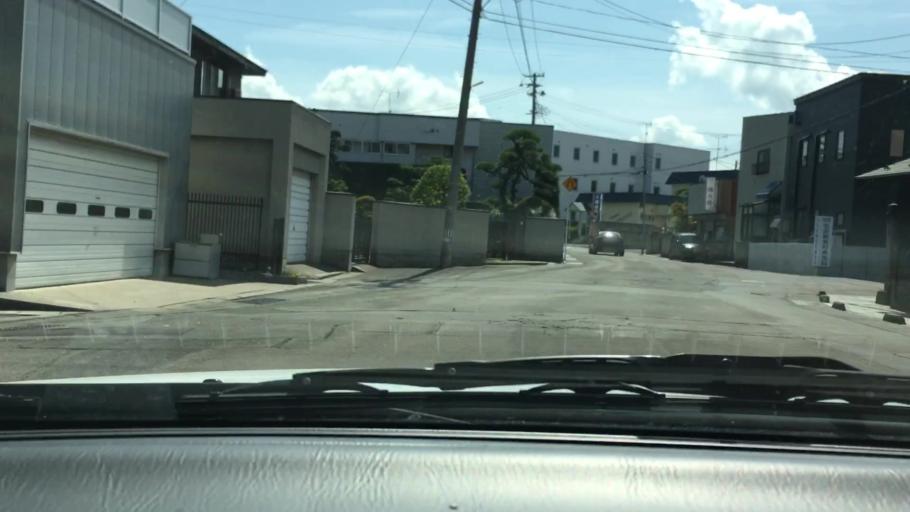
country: JP
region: Aomori
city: Hirosaki
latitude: 40.5957
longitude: 140.4713
